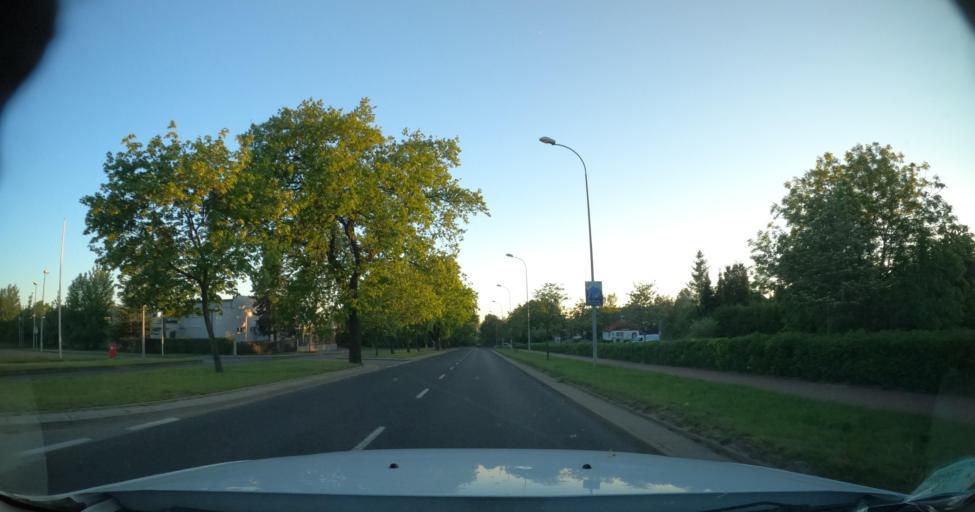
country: PL
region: Pomeranian Voivodeship
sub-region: Slupsk
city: Slupsk
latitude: 54.4672
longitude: 17.0547
